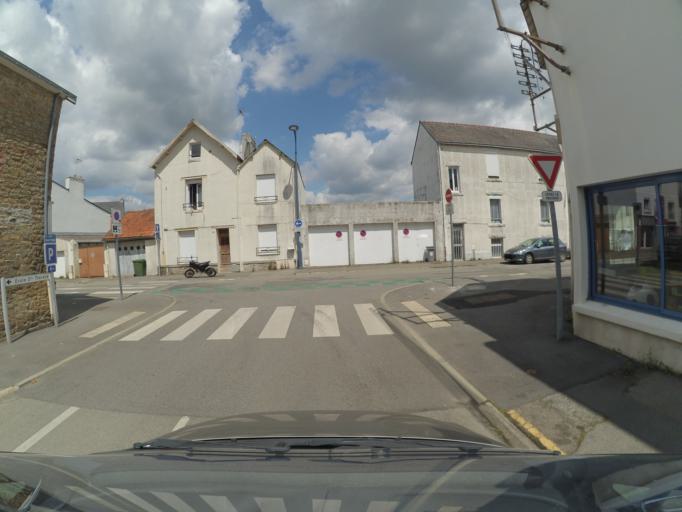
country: FR
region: Brittany
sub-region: Departement du Morbihan
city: Auray
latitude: 47.6788
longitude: -2.9981
